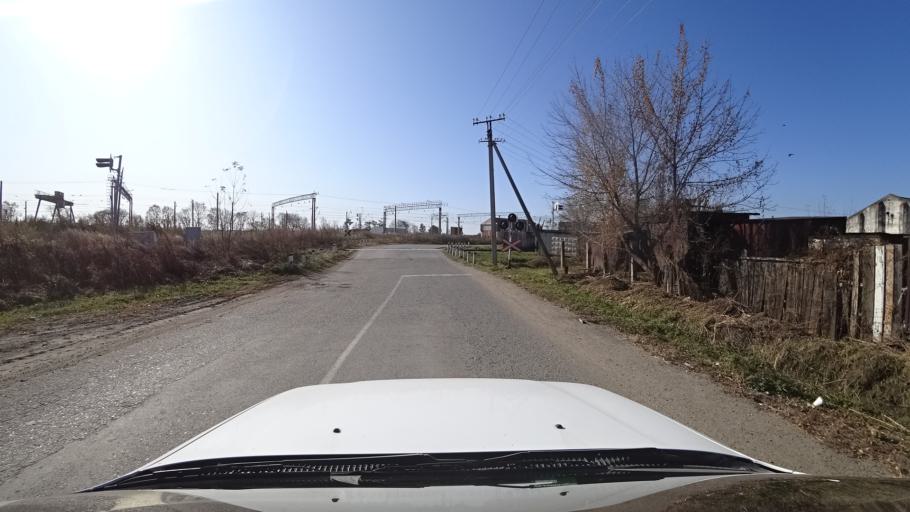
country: RU
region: Primorskiy
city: Dal'nerechensk
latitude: 45.9347
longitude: 133.7183
